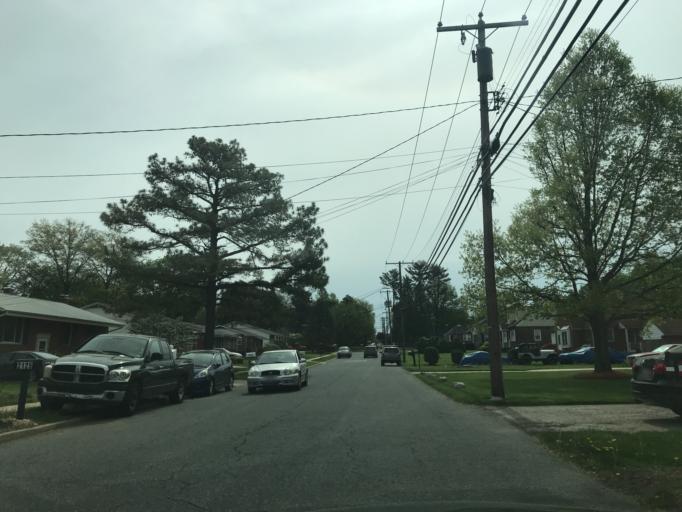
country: US
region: Maryland
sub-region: Howard County
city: Ilchester
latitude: 39.2784
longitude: -76.7667
